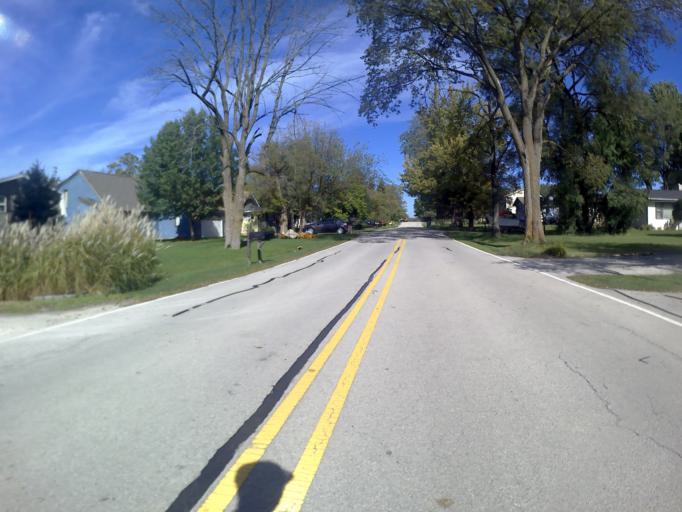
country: US
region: Illinois
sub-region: DuPage County
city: Downers Grove
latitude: 41.7818
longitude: -88.0299
